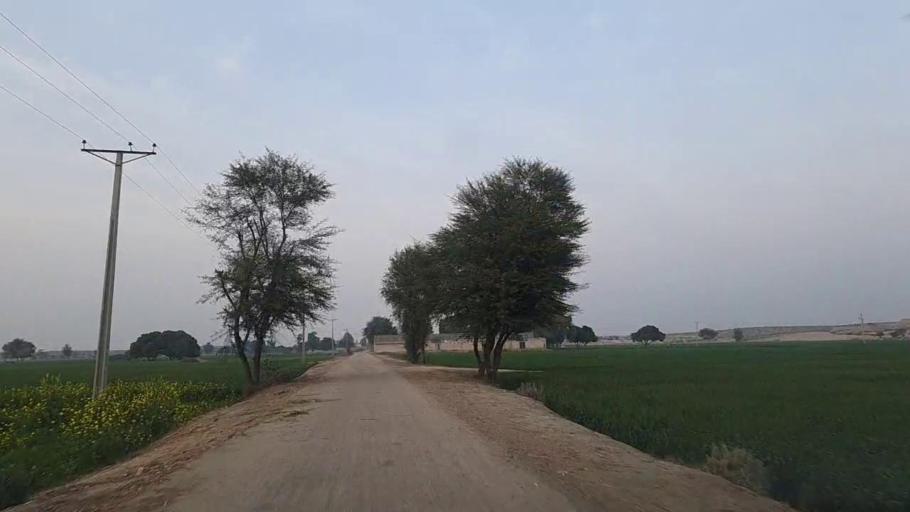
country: PK
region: Sindh
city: Jam Sahib
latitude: 26.4706
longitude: 68.5481
